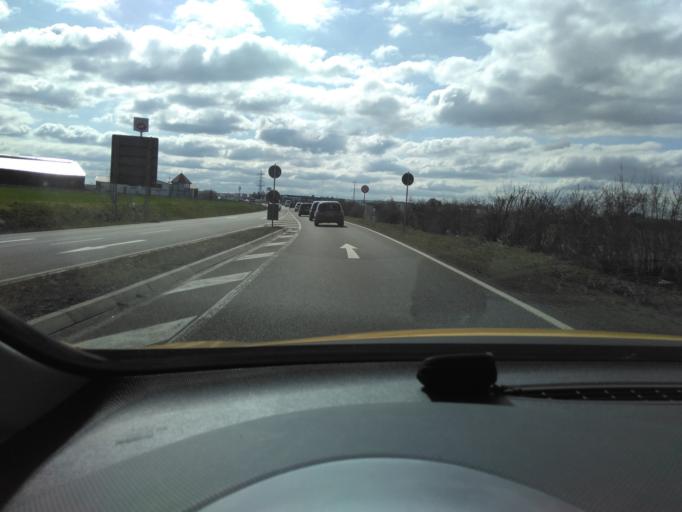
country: DE
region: North Rhine-Westphalia
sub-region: Regierungsbezirk Koln
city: Erftstadt
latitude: 50.8016
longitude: 6.7863
